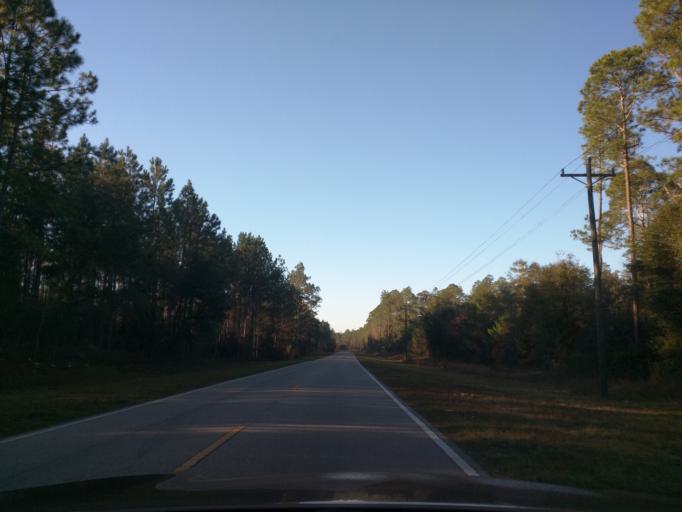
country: US
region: Florida
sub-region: Leon County
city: Woodville
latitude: 30.3584
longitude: -84.1300
